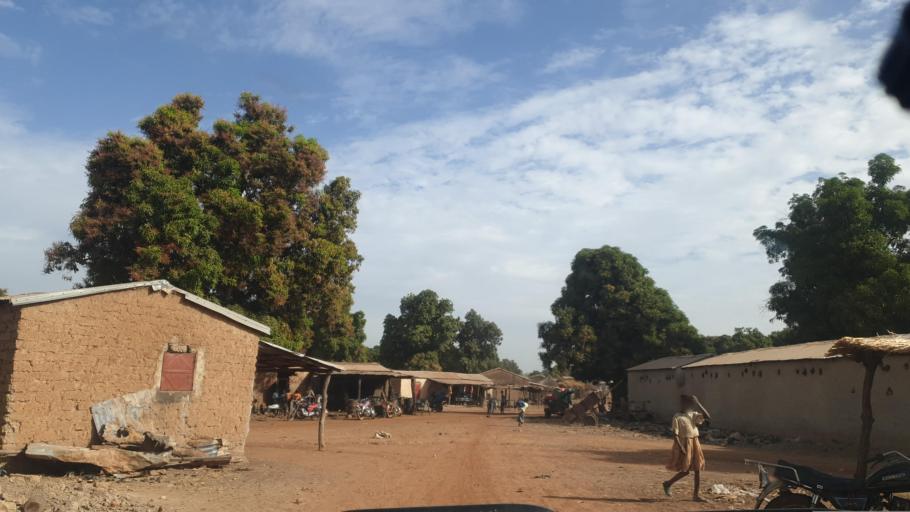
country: ML
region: Sikasso
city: Yanfolila
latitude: 11.4163
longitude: -8.0000
